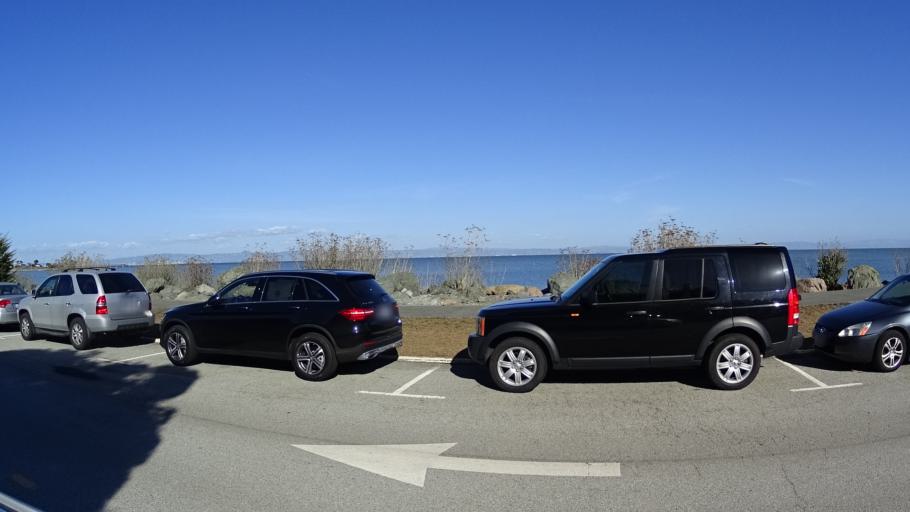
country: US
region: California
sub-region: San Mateo County
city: South San Francisco
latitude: 37.6560
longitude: -122.3769
